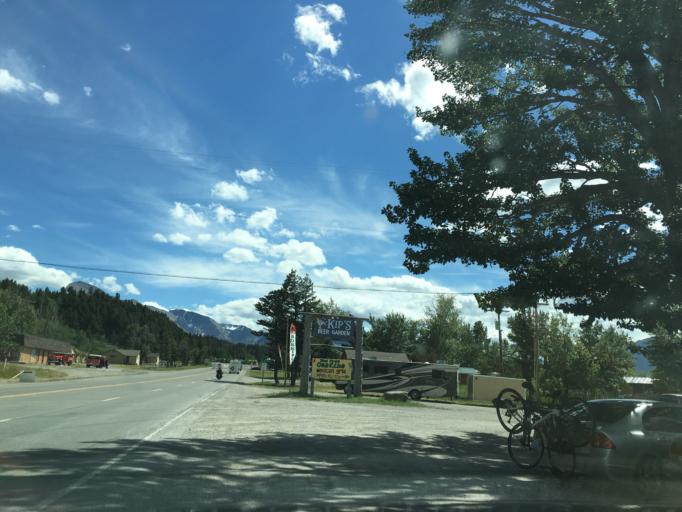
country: US
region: Montana
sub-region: Glacier County
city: North Browning
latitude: 48.7459
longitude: -113.4291
